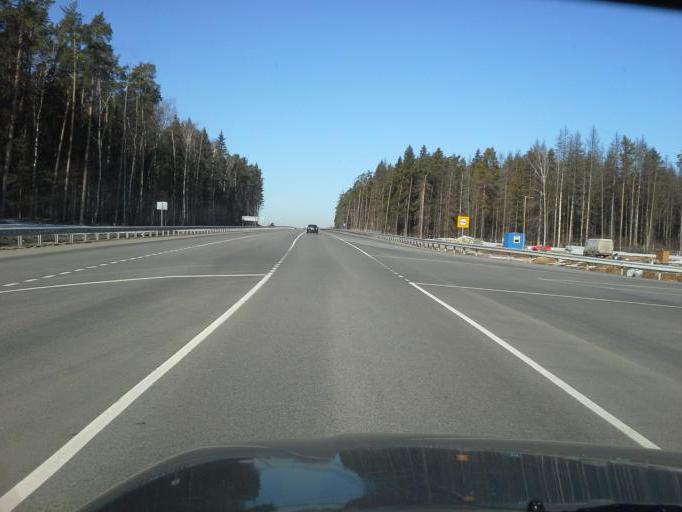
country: RU
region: Moskovskaya
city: Lesnoy Gorodok
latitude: 55.6733
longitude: 37.1704
